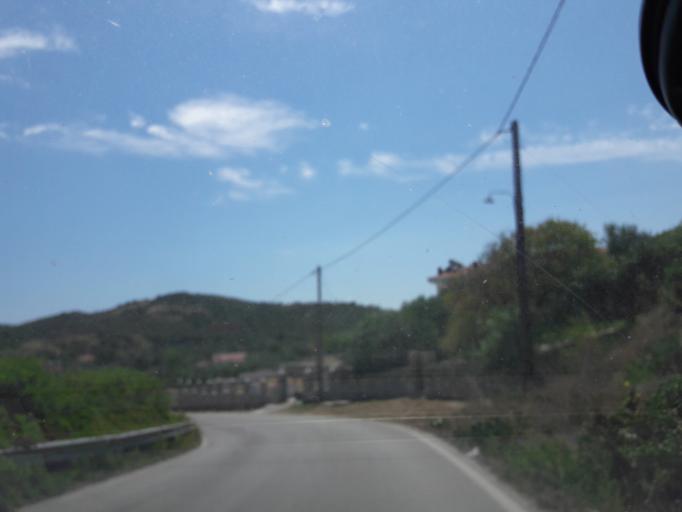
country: GR
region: Central Macedonia
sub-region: Nomos Chalkidikis
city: Nea Roda
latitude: 40.3210
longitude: 23.9216
